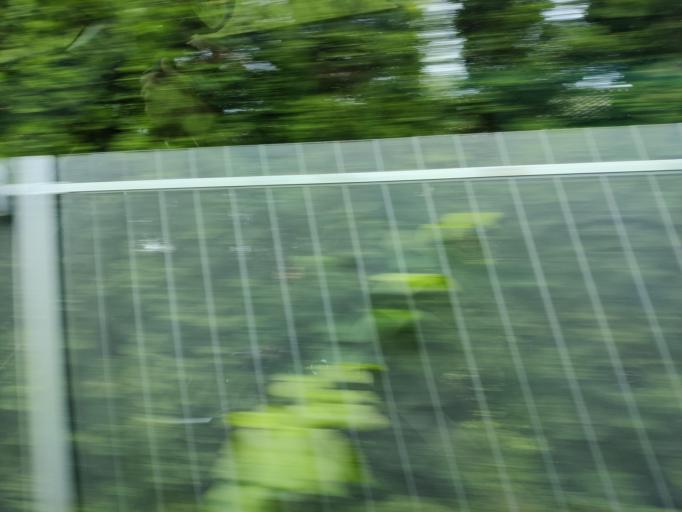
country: PL
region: Masovian Voivodeship
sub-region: Powiat piaseczynski
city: Konstancin-Jeziorna
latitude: 52.1132
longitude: 21.1210
